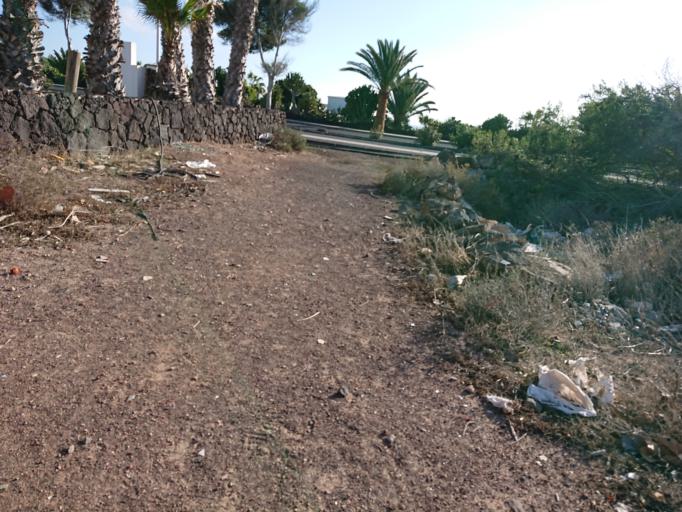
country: ES
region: Canary Islands
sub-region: Provincia de Las Palmas
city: Playa Blanca
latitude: 28.8657
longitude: -13.8481
